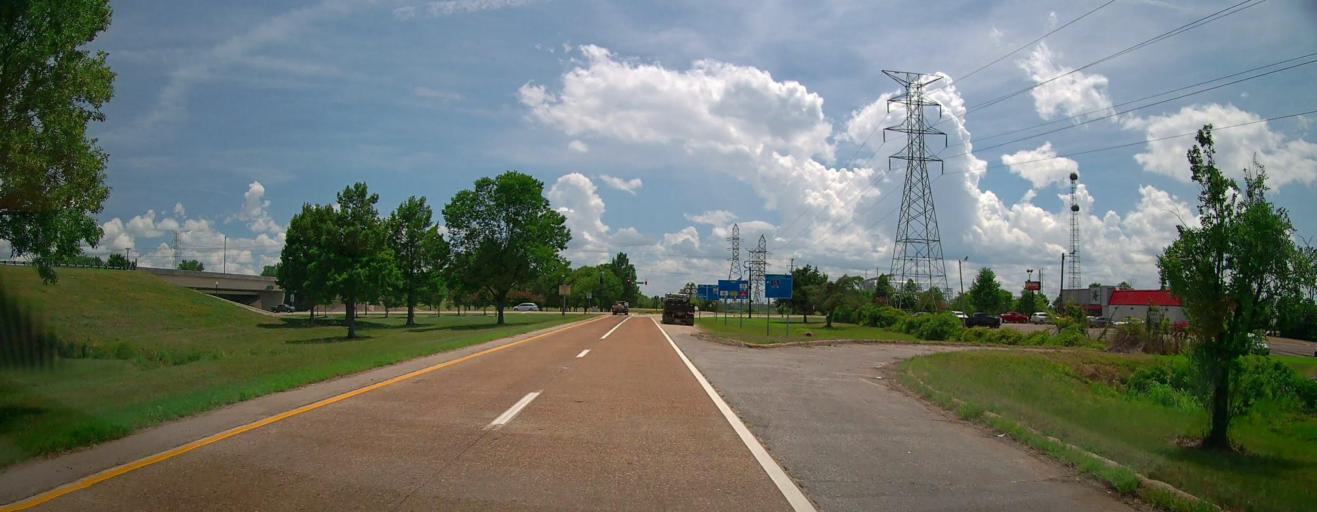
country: US
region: Mississippi
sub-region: Lee County
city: Tupelo
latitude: 34.2590
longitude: -88.6950
